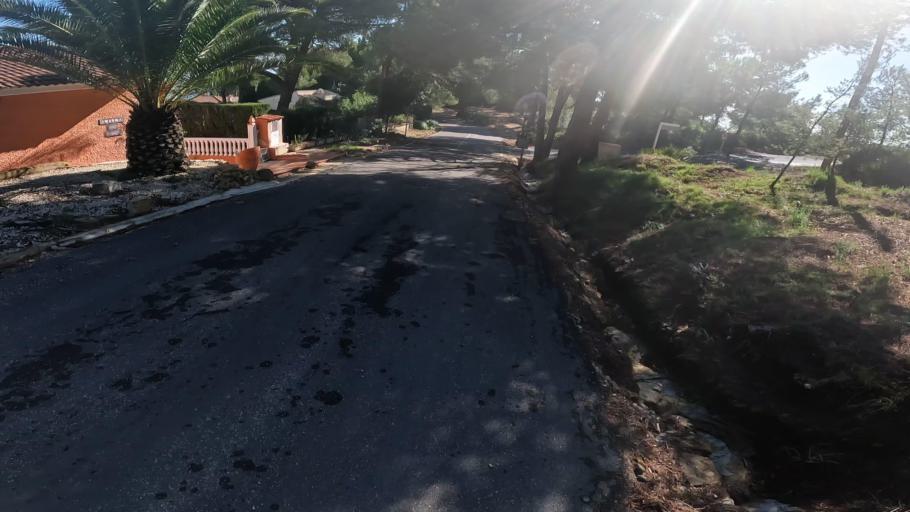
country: ES
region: Valencia
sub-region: Provincia de Castello
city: Alcoceber
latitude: 40.2651
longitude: 0.2729
